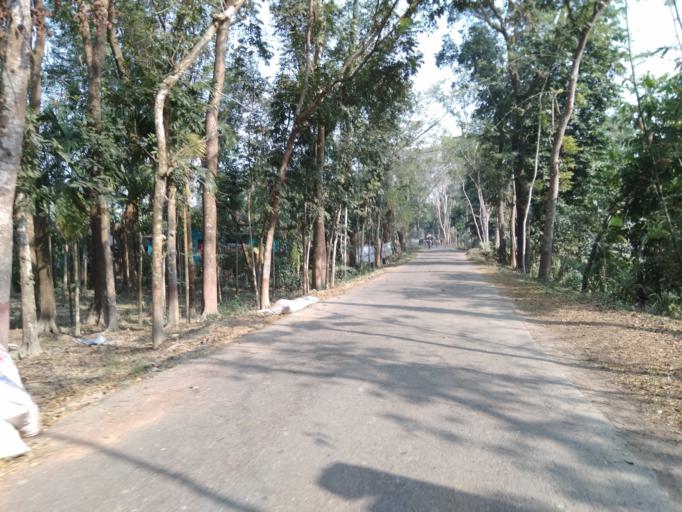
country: BD
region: Barisal
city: Mehendiganj
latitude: 22.9635
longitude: 90.4147
